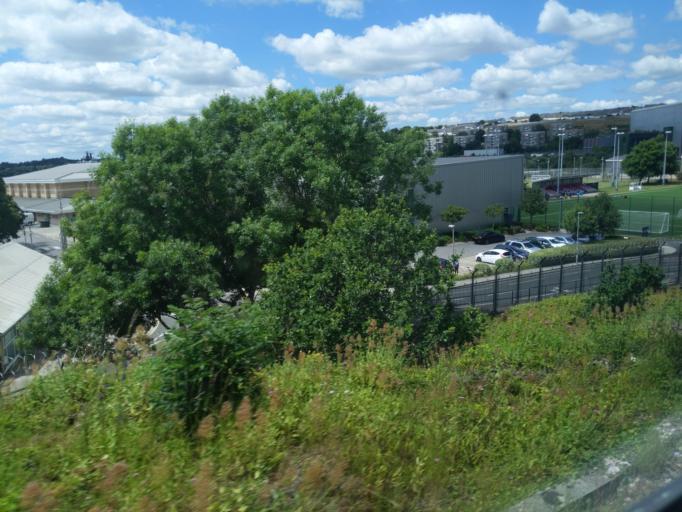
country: GB
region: England
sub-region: Cornwall
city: Torpoint
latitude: 50.3930
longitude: -4.1815
